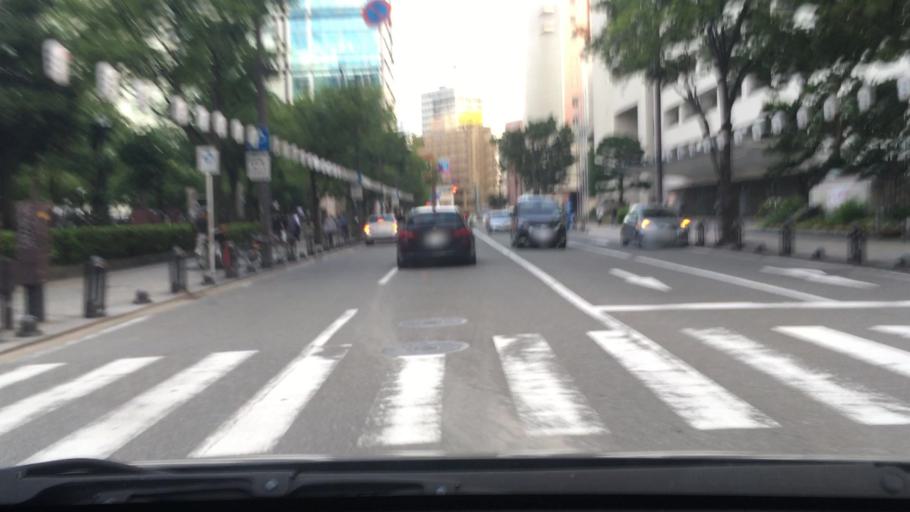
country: JP
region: Fukuoka
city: Fukuoka-shi
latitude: 33.5908
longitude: 130.4020
